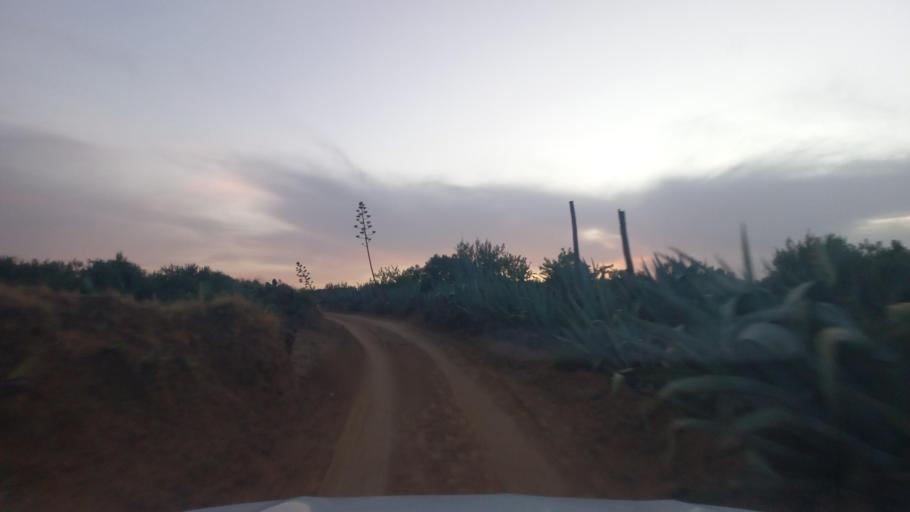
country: TN
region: Al Qasrayn
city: Kasserine
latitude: 35.2312
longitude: 9.0397
